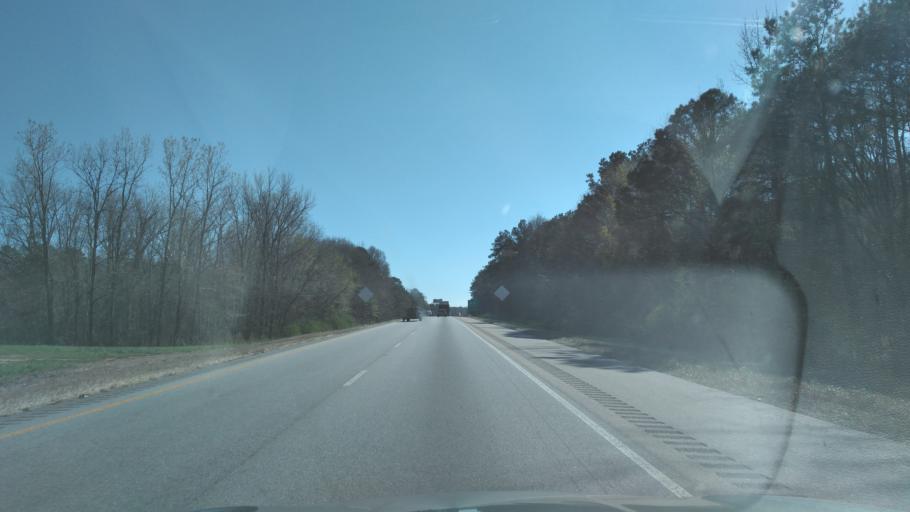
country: US
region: Alabama
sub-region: Lowndes County
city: Fort Deposit
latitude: 32.0000
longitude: -86.5247
